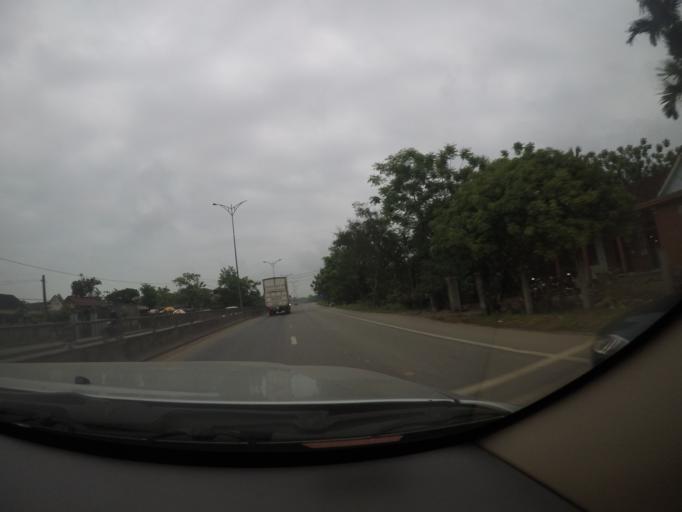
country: VN
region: Thua Thien-Hue
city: Phong Dien
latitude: 16.6018
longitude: 107.3335
